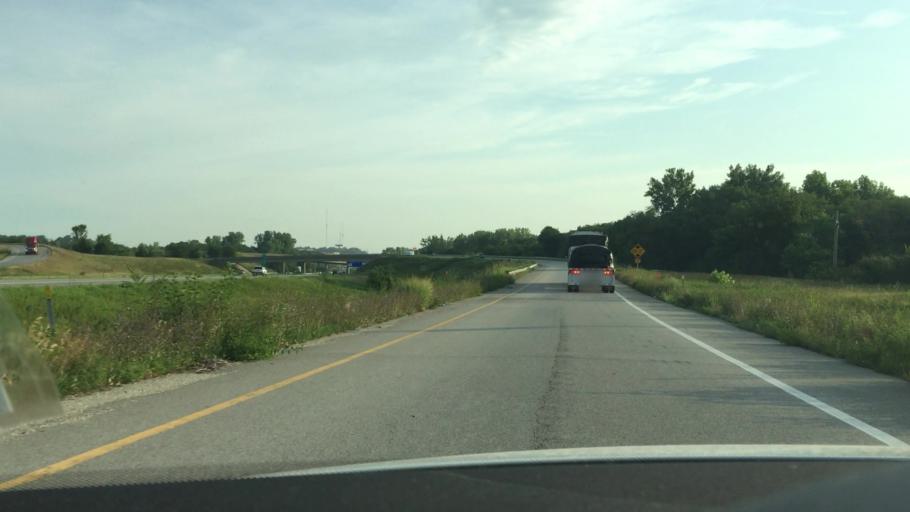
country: US
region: Missouri
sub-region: Buchanan County
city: Saint Joseph
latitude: 39.7044
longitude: -94.7880
